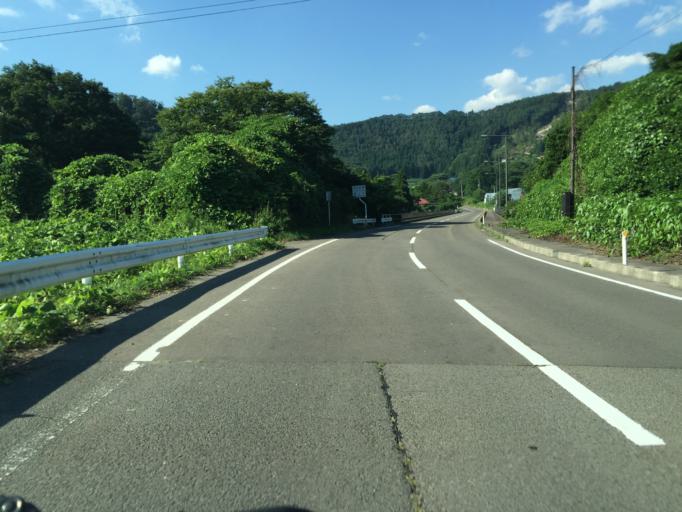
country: JP
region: Fukushima
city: Hobaramachi
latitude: 37.8877
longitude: 140.4346
